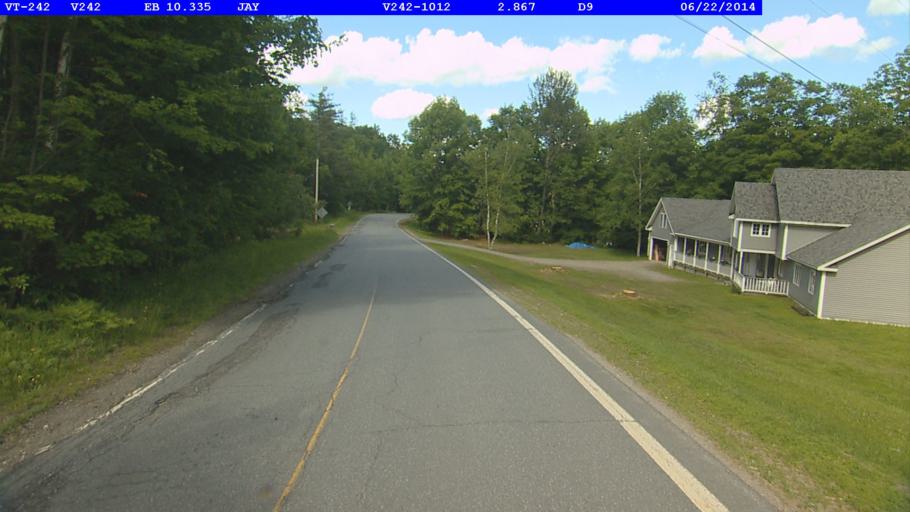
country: US
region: Vermont
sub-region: Franklin County
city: Richford
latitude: 44.9397
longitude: -72.4573
